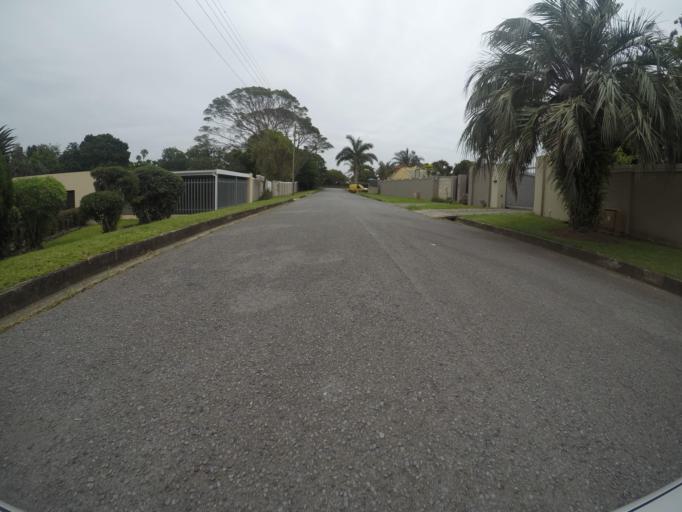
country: ZA
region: Eastern Cape
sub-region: Buffalo City Metropolitan Municipality
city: East London
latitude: -32.9763
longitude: 27.9363
